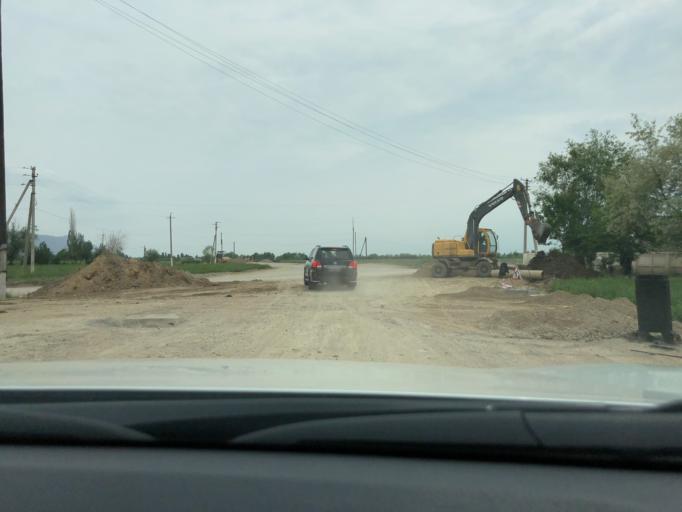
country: TJ
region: Viloyati Sughd
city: Isfara
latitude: 40.1521
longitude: 70.6224
